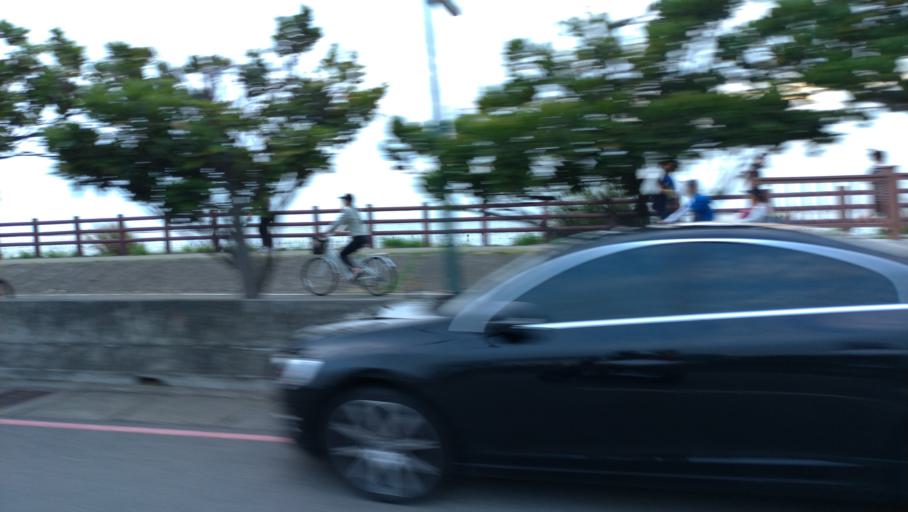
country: TW
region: Taiwan
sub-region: Hsinchu
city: Hsinchu
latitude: 24.7776
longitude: 120.9144
